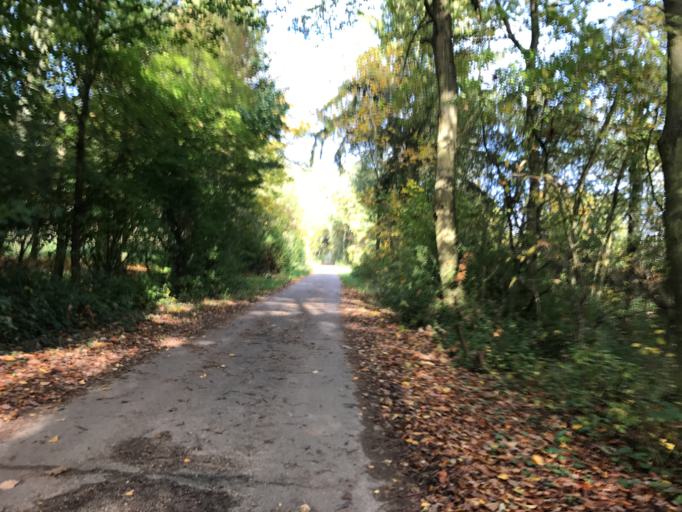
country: DE
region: Rheinland-Pfalz
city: Aspisheim
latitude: 49.9230
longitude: 7.9844
